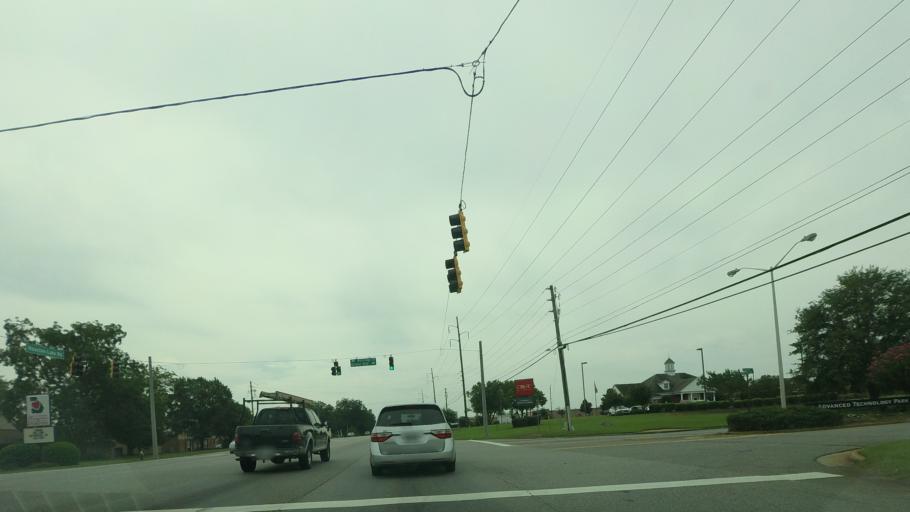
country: US
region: Georgia
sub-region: Houston County
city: Centerville
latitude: 32.6151
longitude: -83.6810
